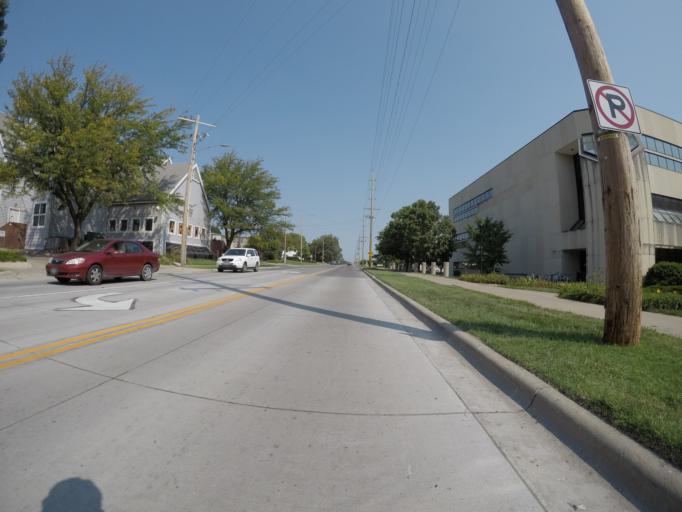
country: US
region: Kansas
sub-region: Riley County
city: Manhattan
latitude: 39.1932
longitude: -96.5854
